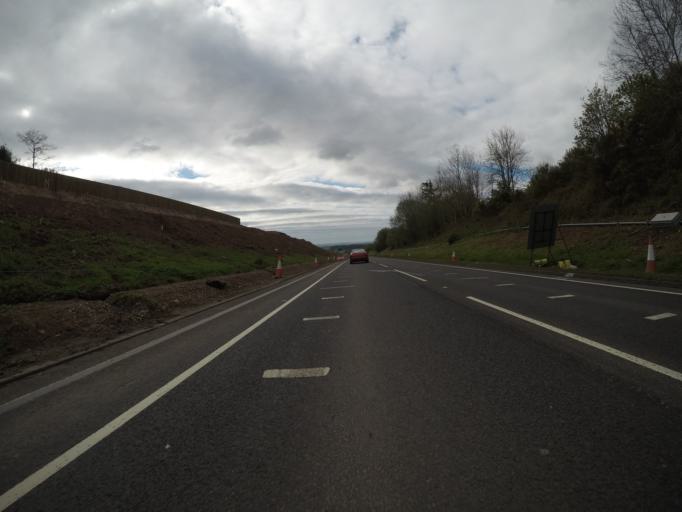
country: GB
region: Scotland
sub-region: Perth and Kinross
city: Bankfoot
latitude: 56.5029
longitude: -3.5104
